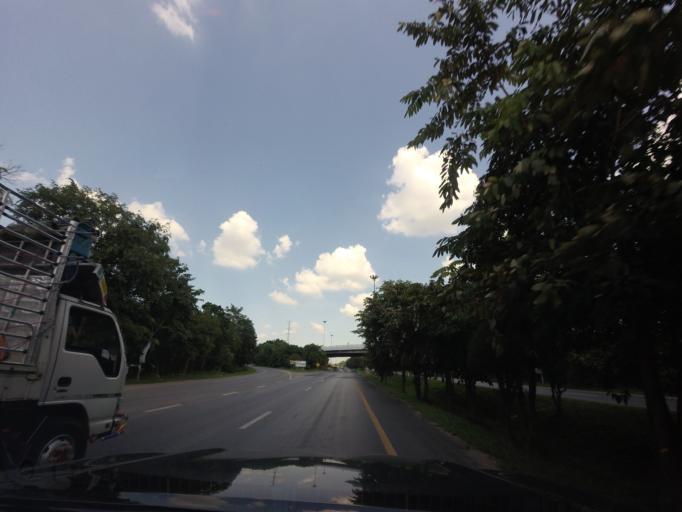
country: TH
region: Nakhon Ratchasima
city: Nakhon Ratchasima
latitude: 15.0562
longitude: 102.1569
